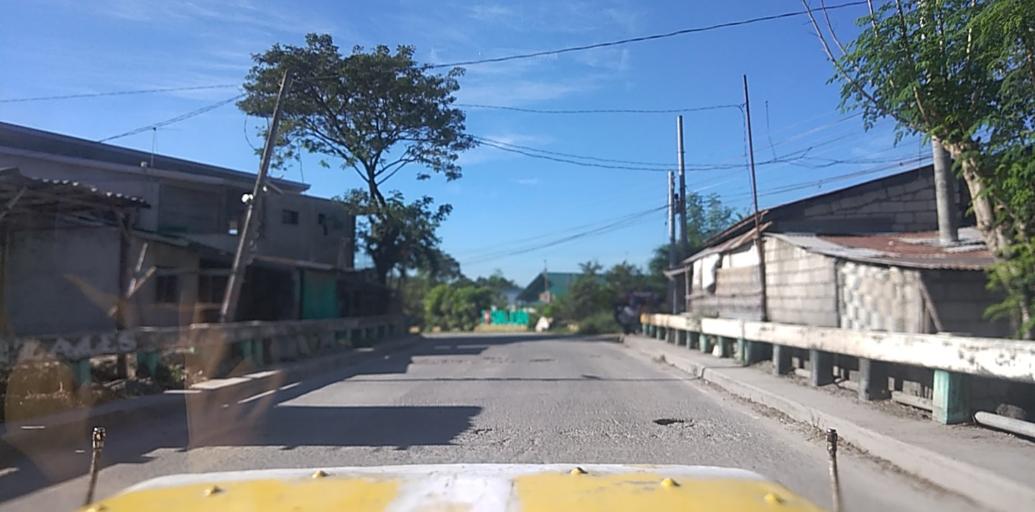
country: PH
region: Central Luzon
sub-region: Province of Pampanga
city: Anao
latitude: 15.1180
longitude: 120.7026
